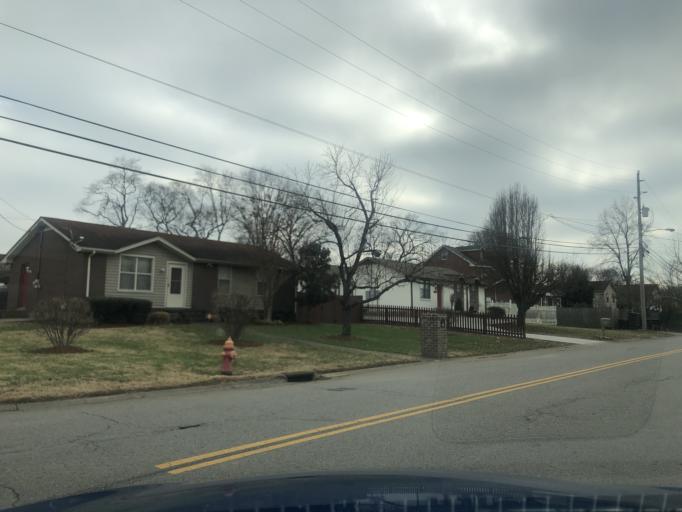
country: US
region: Tennessee
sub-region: Davidson County
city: Oak Hill
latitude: 36.0944
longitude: -86.7101
